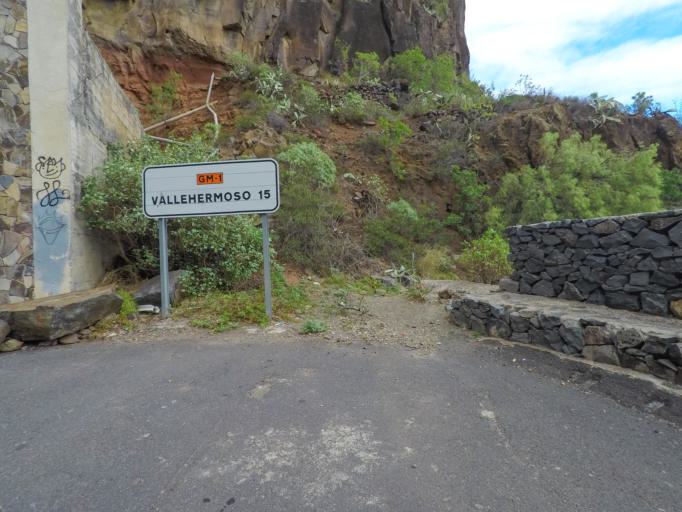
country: ES
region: Canary Islands
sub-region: Provincia de Santa Cruz de Tenerife
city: Agulo
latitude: 28.1912
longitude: -17.1976
